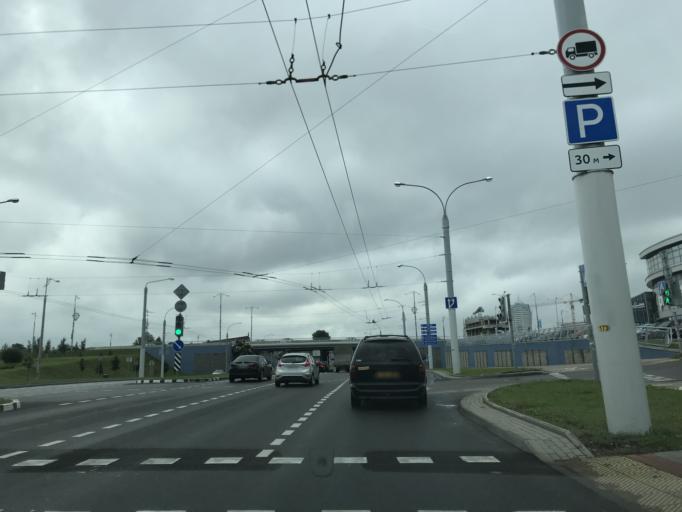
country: BY
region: Minsk
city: Minsk
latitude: 53.9324
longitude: 27.6381
